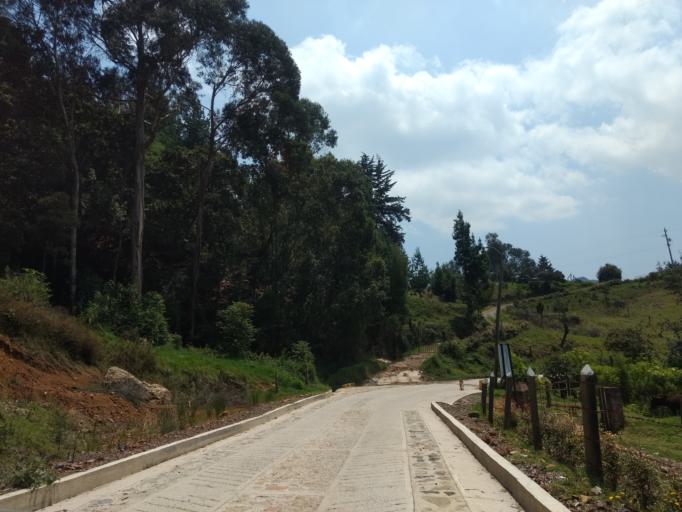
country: CO
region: Boyaca
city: Raquira
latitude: 5.5059
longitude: -73.7137
